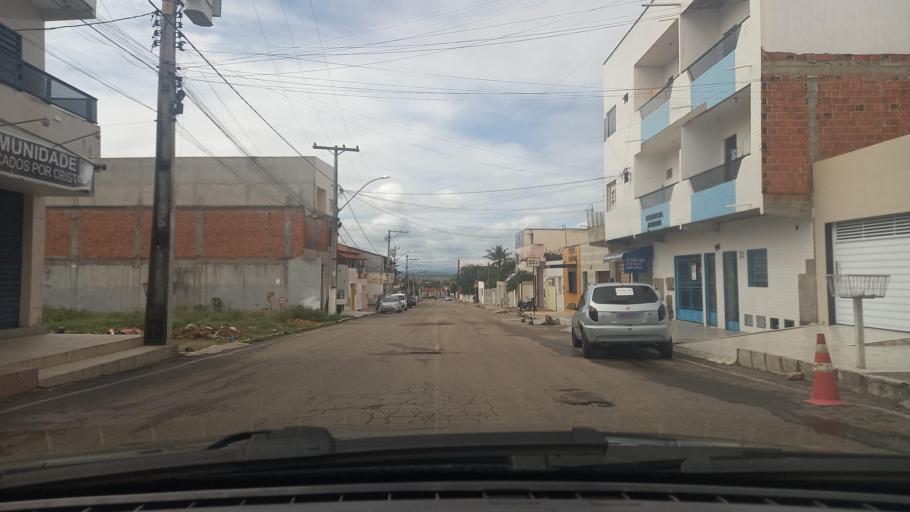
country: BR
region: Bahia
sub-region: Paulo Afonso
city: Paulo Afonso
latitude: -9.4459
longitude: -38.2212
